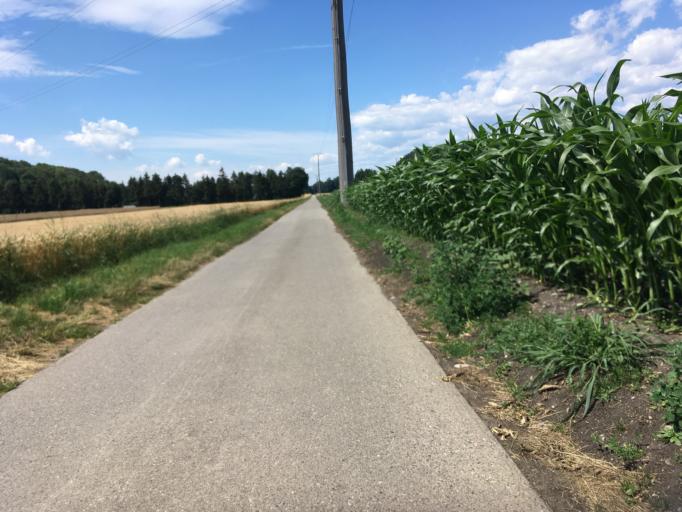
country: CH
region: Fribourg
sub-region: See District
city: Bas-Vully
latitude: 46.9618
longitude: 7.0449
